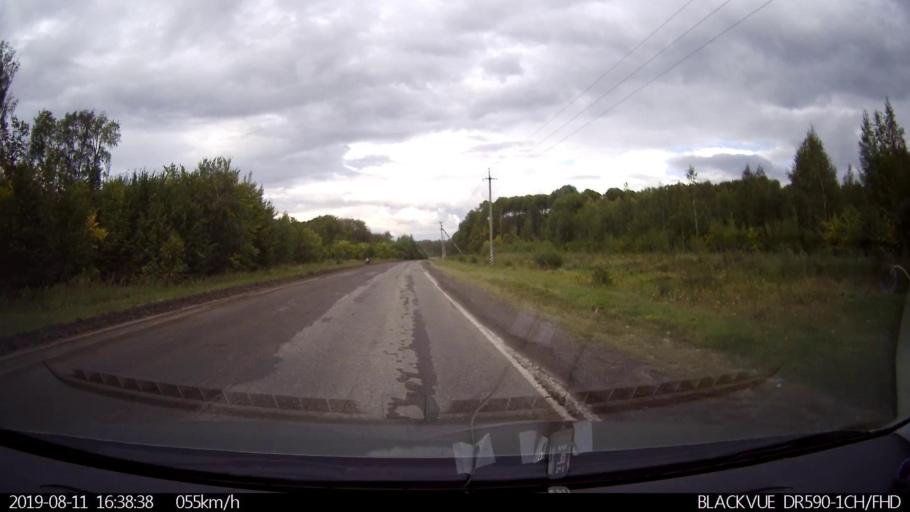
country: RU
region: Ulyanovsk
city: Mayna
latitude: 54.1359
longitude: 47.6277
